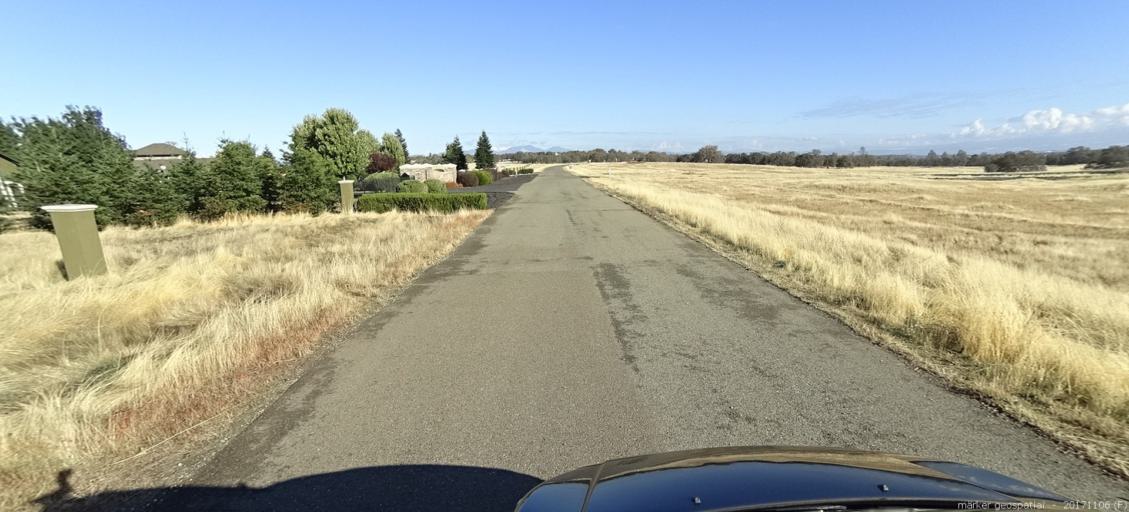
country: US
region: California
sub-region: Shasta County
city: Palo Cedro
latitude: 40.4960
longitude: -122.2464
